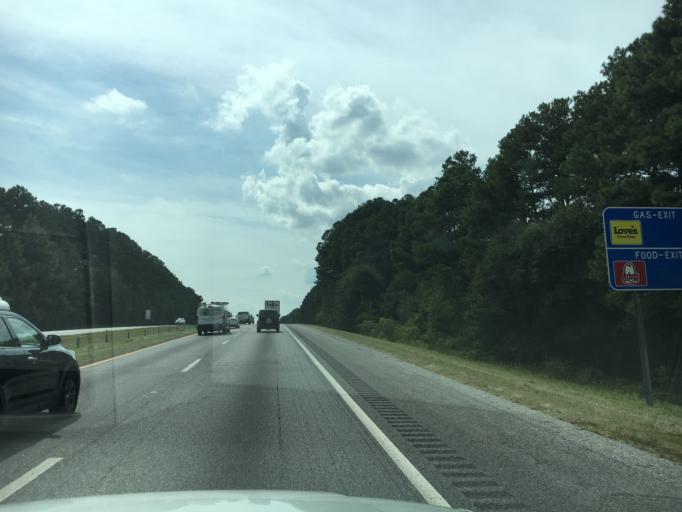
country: US
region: Georgia
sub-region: Hart County
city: Reed Creek
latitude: 34.5096
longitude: -82.9507
